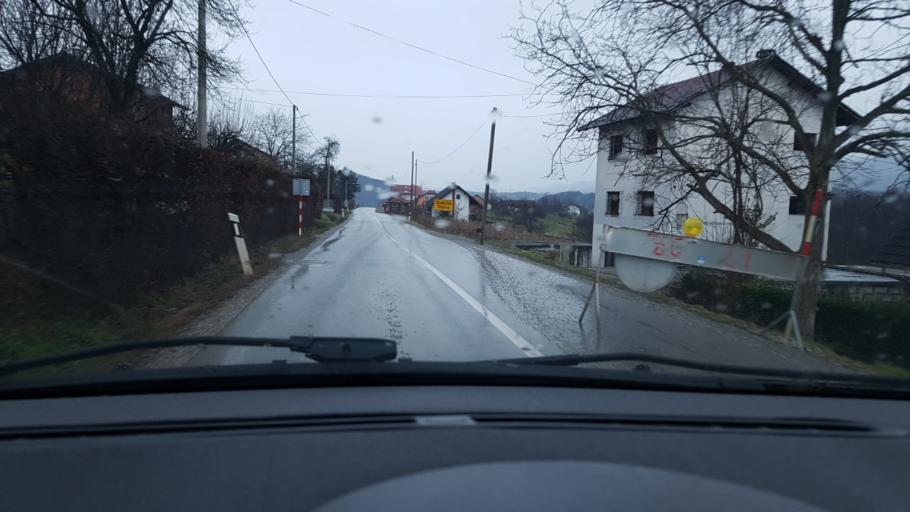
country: HR
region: Krapinsko-Zagorska
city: Oroslavje
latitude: 45.9778
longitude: 15.9113
